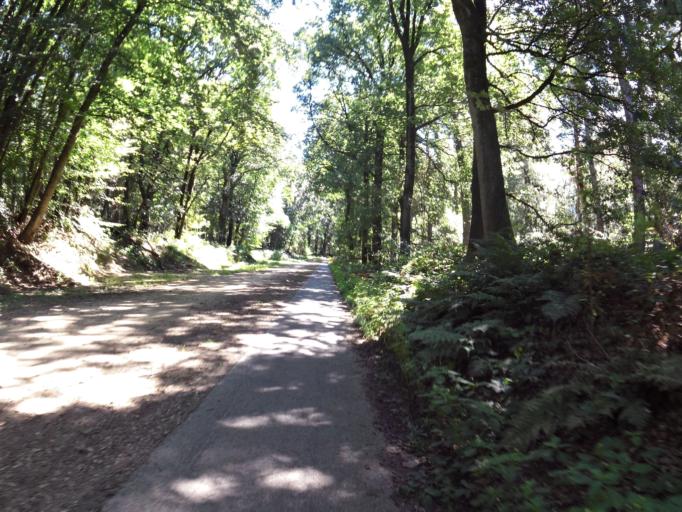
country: NL
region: Gelderland
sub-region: Gemeente Groesbeek
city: Berg en Dal
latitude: 51.7966
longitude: 5.8864
